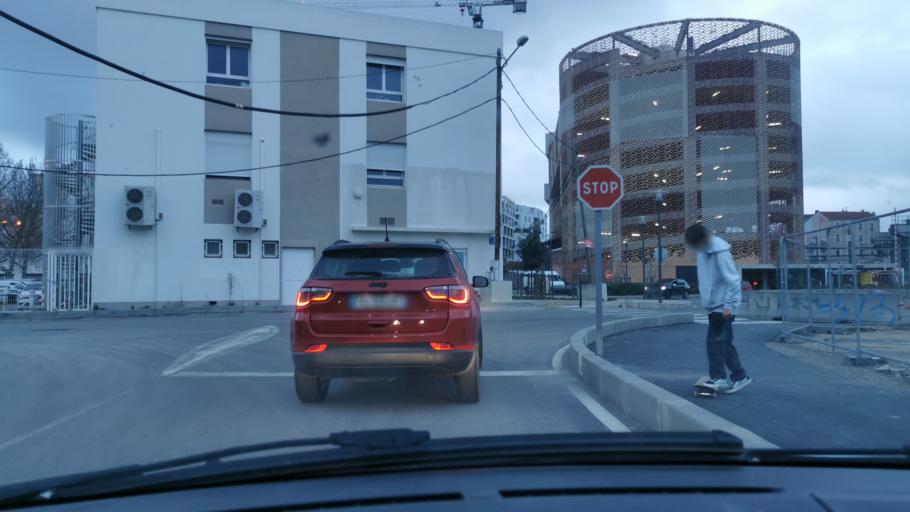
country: FR
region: Languedoc-Roussillon
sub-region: Departement de l'Herault
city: Montpellier
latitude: 43.6021
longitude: 3.8769
